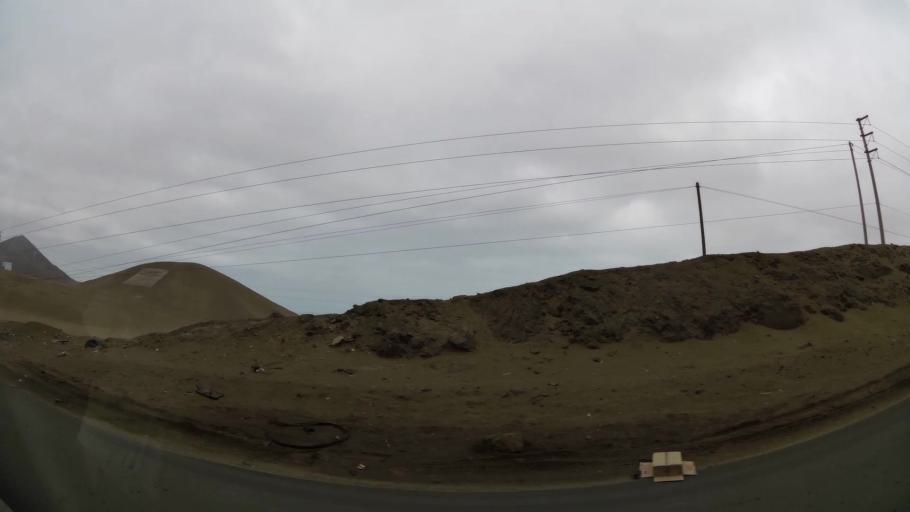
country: PE
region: Lima
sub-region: Lima
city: San Bartolo
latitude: -12.4383
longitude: -76.7559
